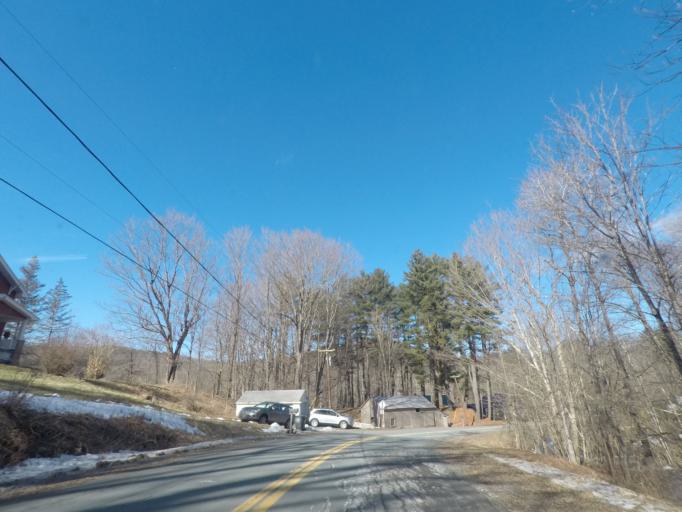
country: US
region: Massachusetts
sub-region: Berkshire County
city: Williamstown
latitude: 42.7463
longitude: -73.3424
